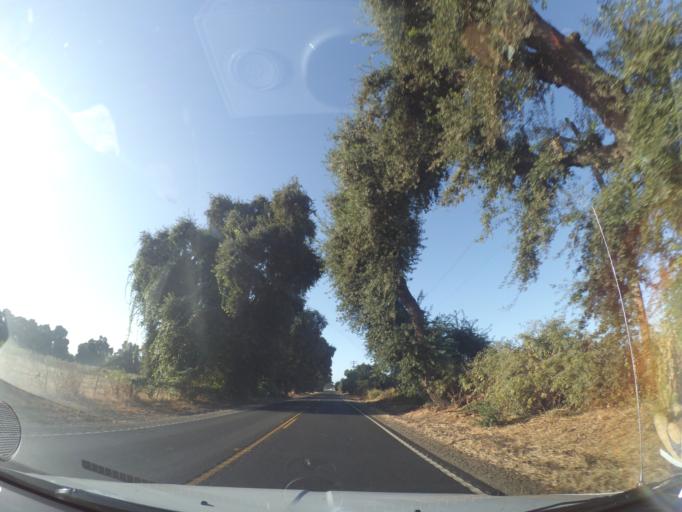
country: US
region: California
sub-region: Merced County
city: Winton
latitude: 37.4783
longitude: -120.5031
